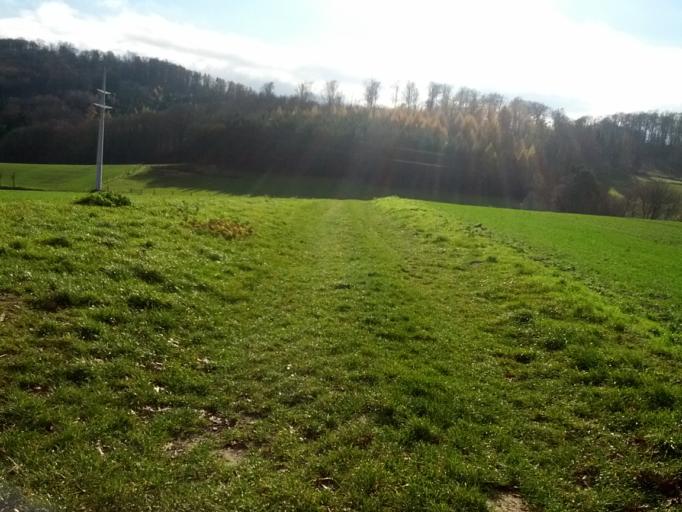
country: DE
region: Thuringia
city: Krauthausen
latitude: 50.9946
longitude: 10.2285
